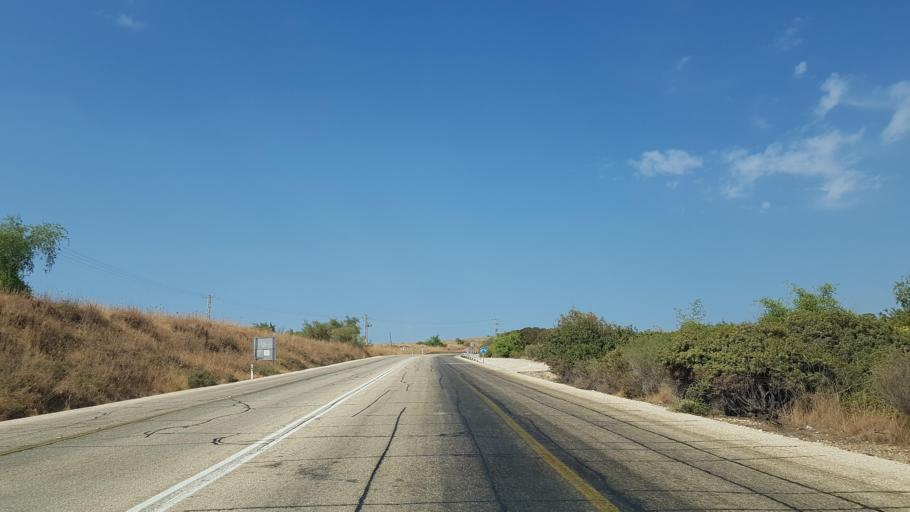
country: SY
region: Quneitra
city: Al Butayhah
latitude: 32.9049
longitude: 35.5976
